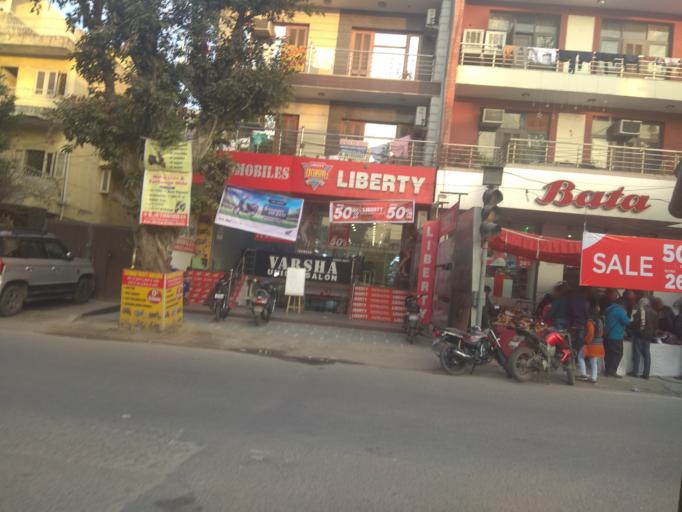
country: IN
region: NCT
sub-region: West Delhi
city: Nangloi Jat
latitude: 28.6344
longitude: 77.0688
